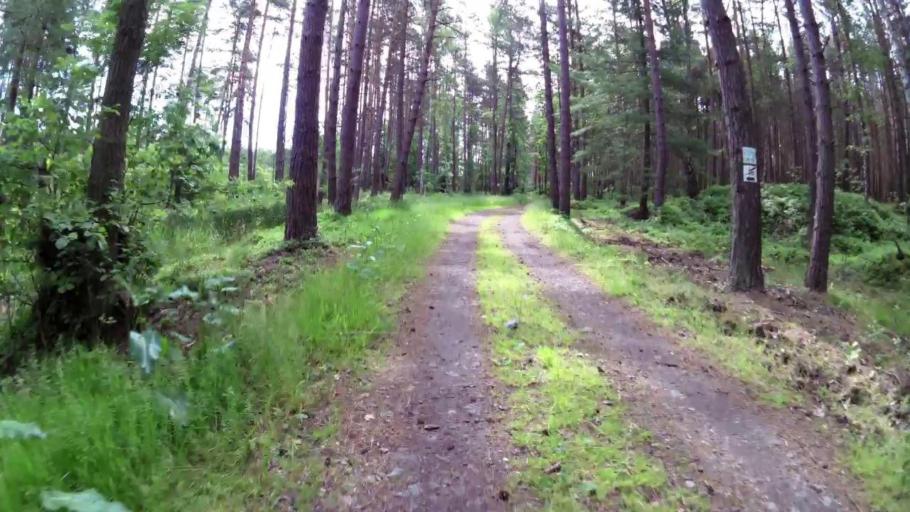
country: PL
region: West Pomeranian Voivodeship
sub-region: Swinoujscie
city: Swinoujscie
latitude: 53.9092
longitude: 14.3151
